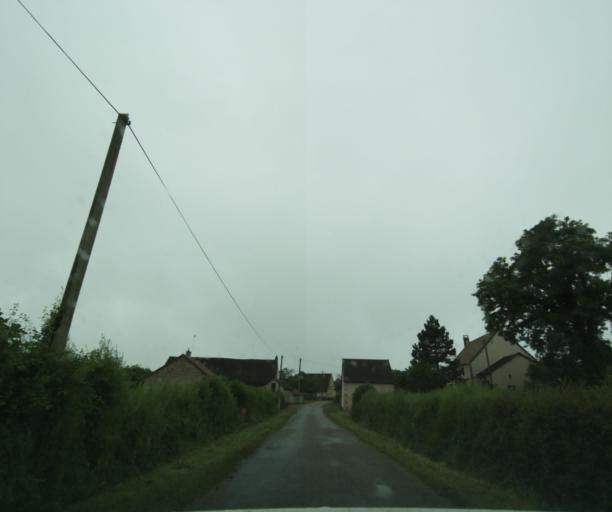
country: FR
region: Bourgogne
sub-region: Departement de Saone-et-Loire
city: Charolles
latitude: 46.4274
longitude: 4.3559
